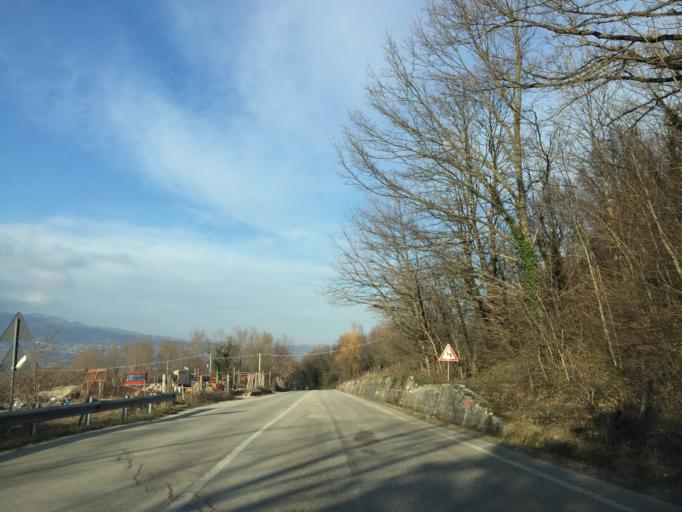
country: IT
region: Molise
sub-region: Provincia di Campobasso
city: San Massimo
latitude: 41.4867
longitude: 14.4047
